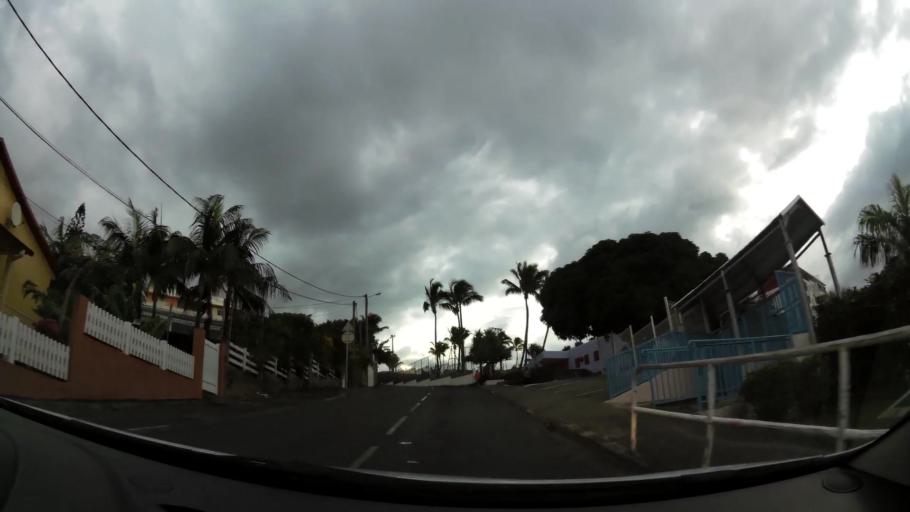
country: RE
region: Reunion
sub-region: Reunion
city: Saint-Denis
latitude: -20.9003
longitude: 55.4703
